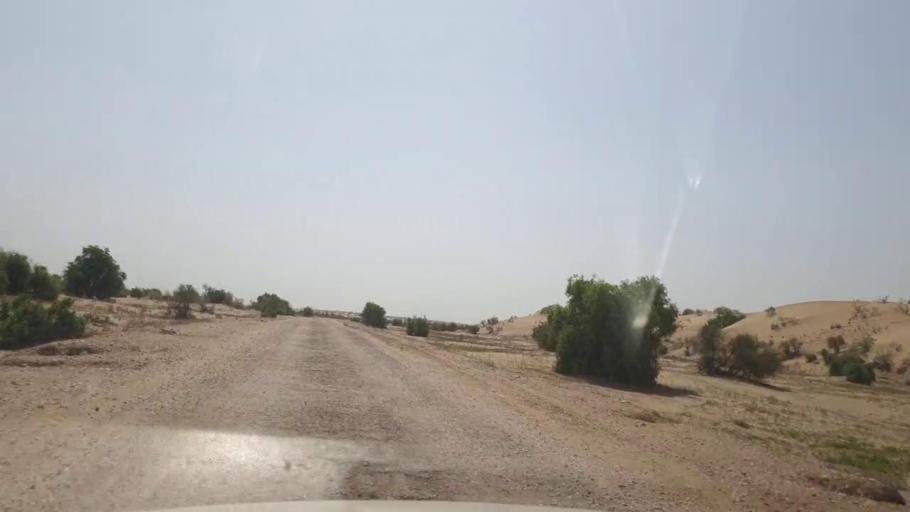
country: PK
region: Sindh
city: Khanpur
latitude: 27.4090
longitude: 69.3203
